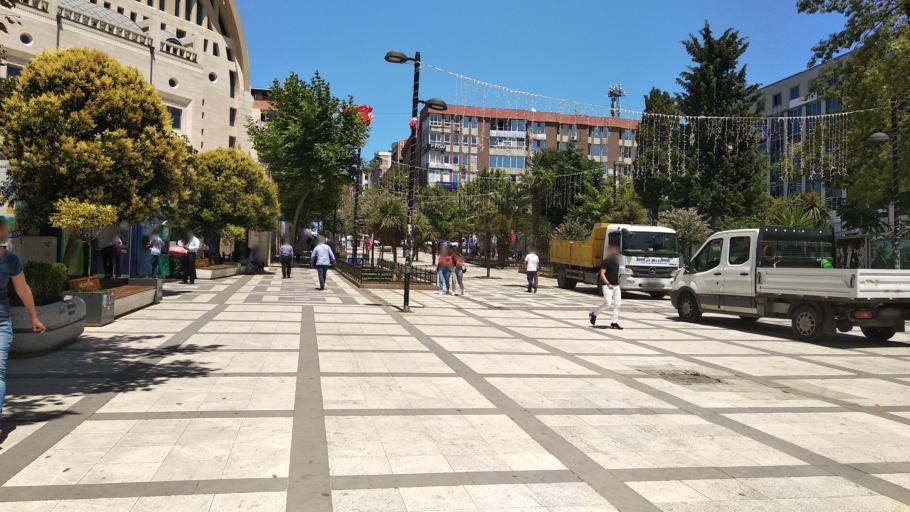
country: TR
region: Istanbul
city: Yakuplu
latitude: 40.9791
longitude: 28.7213
